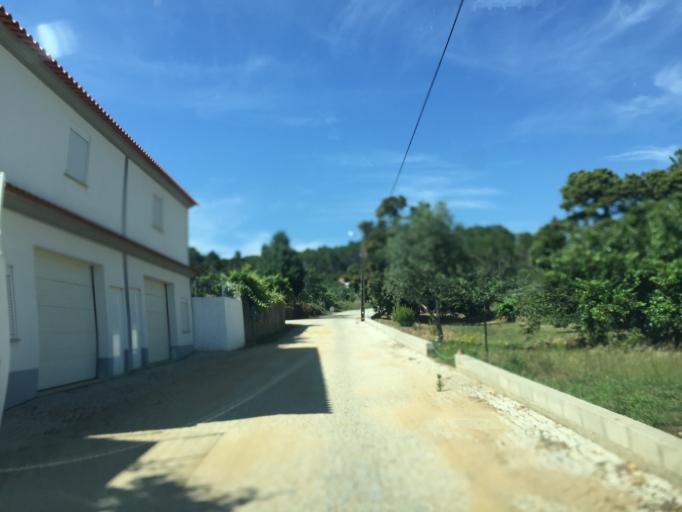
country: PT
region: Castelo Branco
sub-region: Oleiros
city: Oleiros
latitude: 39.9724
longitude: -7.8422
